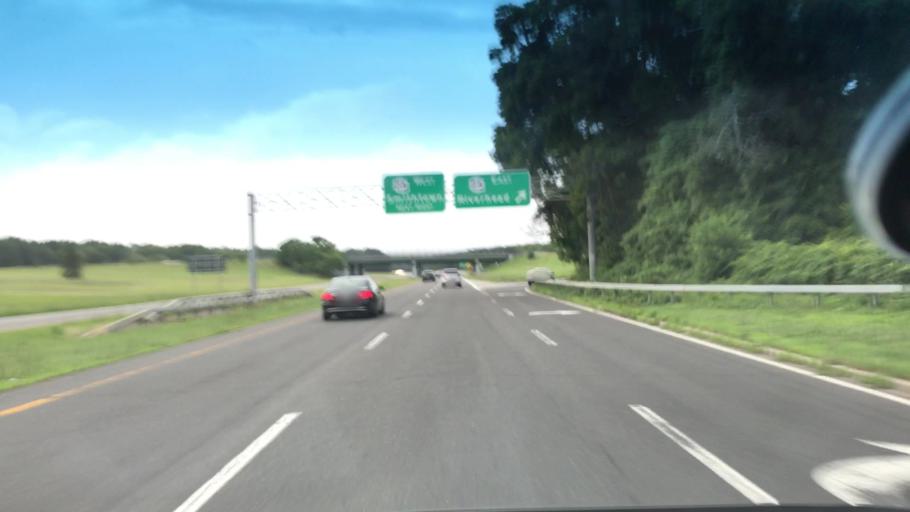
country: US
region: New York
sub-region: Suffolk County
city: Ridge
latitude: 40.8935
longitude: -72.8837
